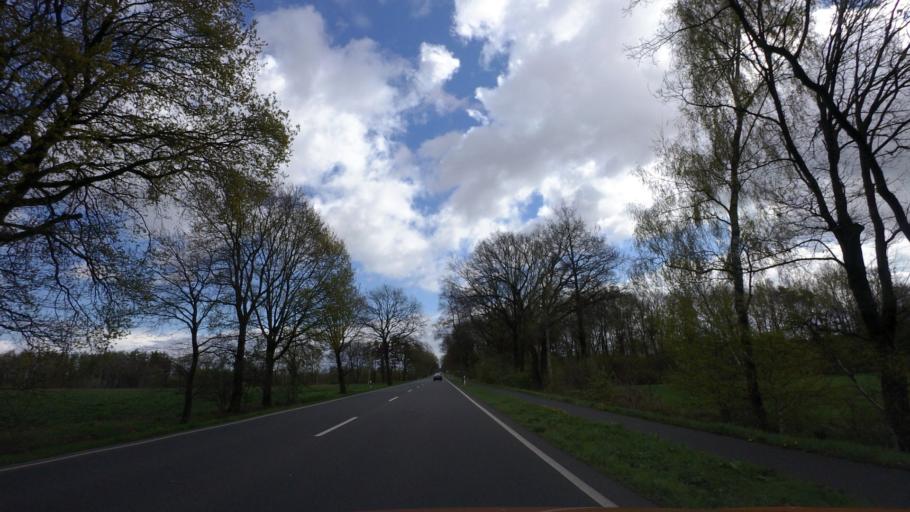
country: DE
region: Lower Saxony
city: Hassendorf
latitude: 53.1197
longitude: 9.2929
